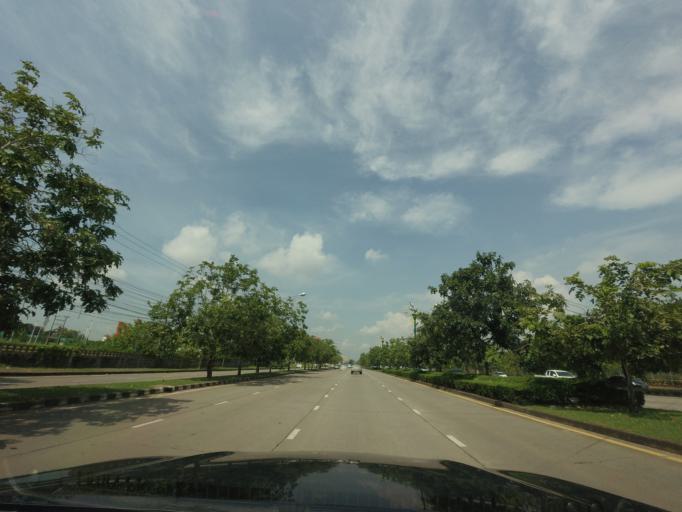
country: TH
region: Khon Kaen
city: Khon Kaen
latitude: 16.4421
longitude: 102.8109
